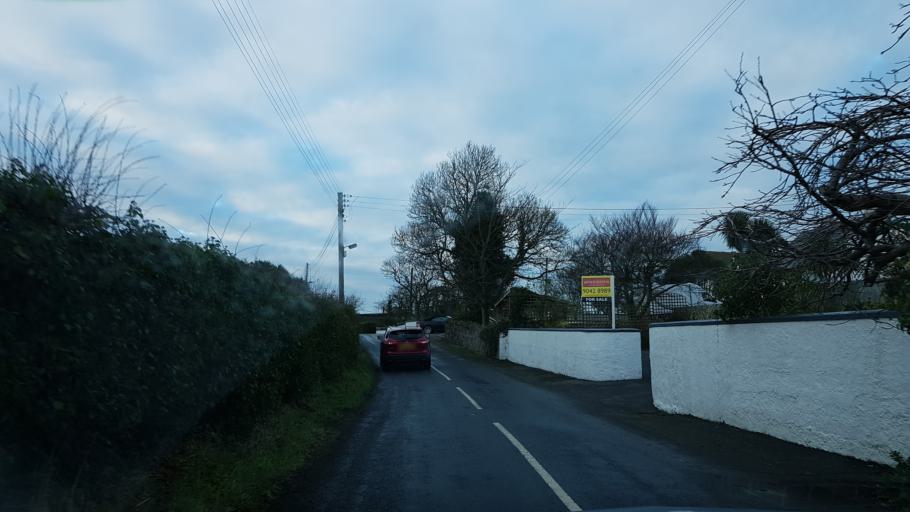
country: GB
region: Northern Ireland
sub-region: Down District
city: Donaghadee
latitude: 54.6710
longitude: -5.5801
